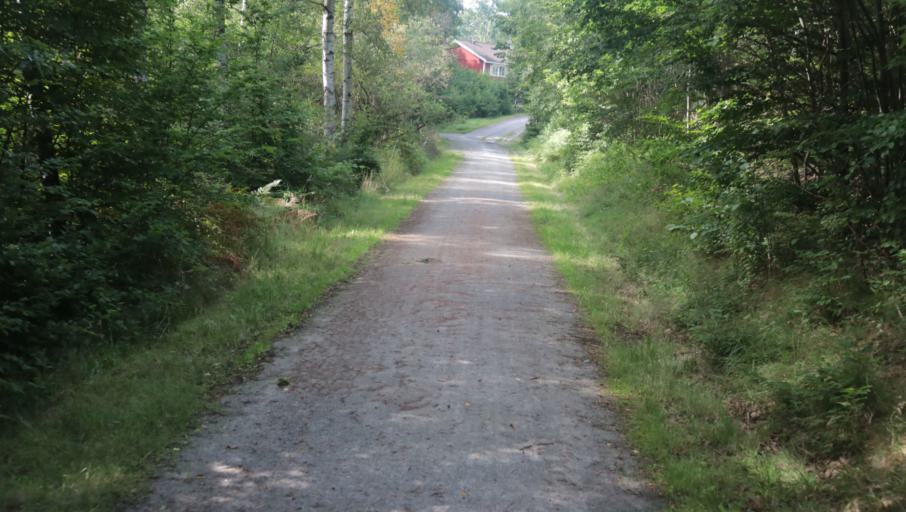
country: SE
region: Blekinge
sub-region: Karlshamns Kommun
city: Karlshamn
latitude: 56.2036
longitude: 14.8622
